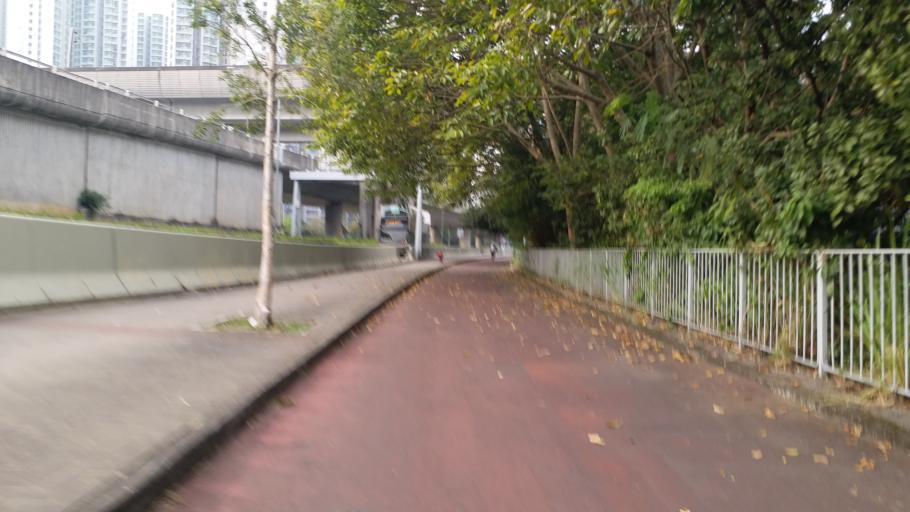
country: HK
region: Yuen Long
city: Yuen Long Kau Hui
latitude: 22.4505
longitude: 114.0096
